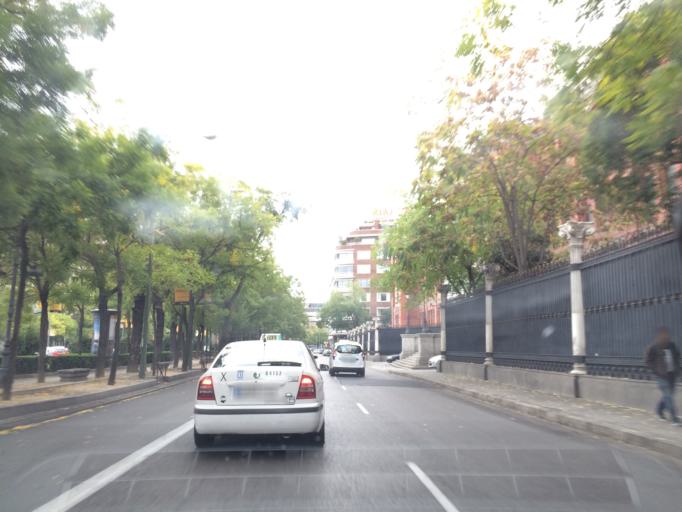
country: ES
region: Madrid
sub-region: Provincia de Madrid
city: Chamberi
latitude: 40.4406
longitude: -3.6920
